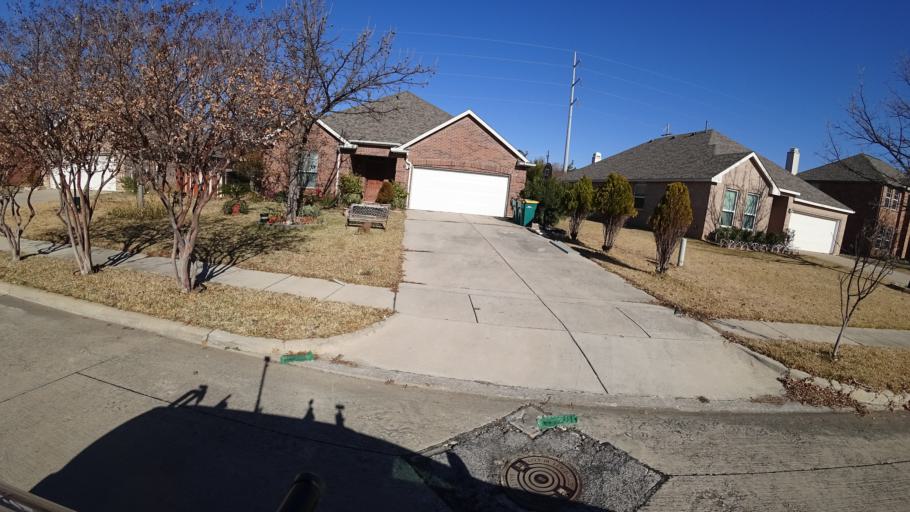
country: US
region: Texas
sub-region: Denton County
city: Lewisville
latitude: 33.0271
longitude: -97.0204
